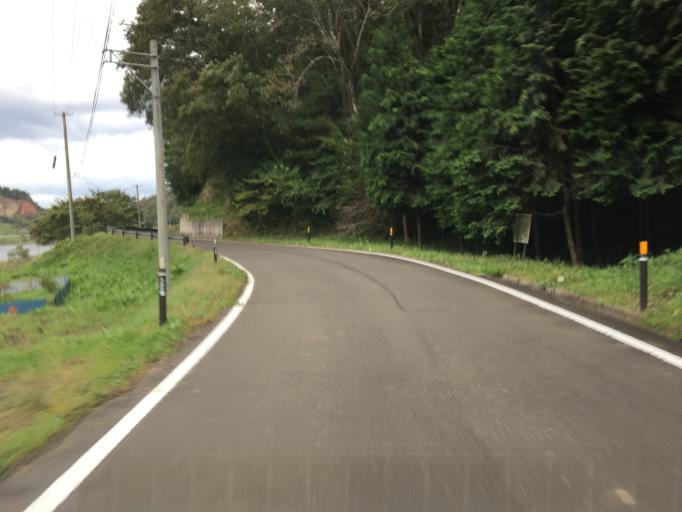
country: JP
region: Miyagi
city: Marumori
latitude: 37.9247
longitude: 140.7476
